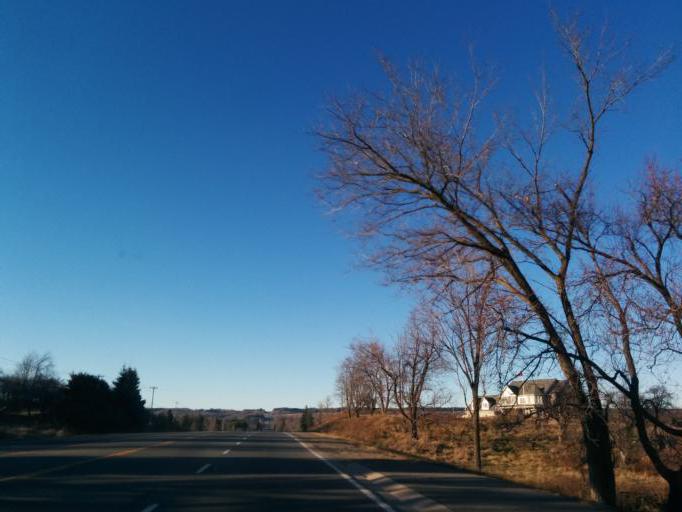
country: CA
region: Ontario
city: Orangeville
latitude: 43.8154
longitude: -79.9351
